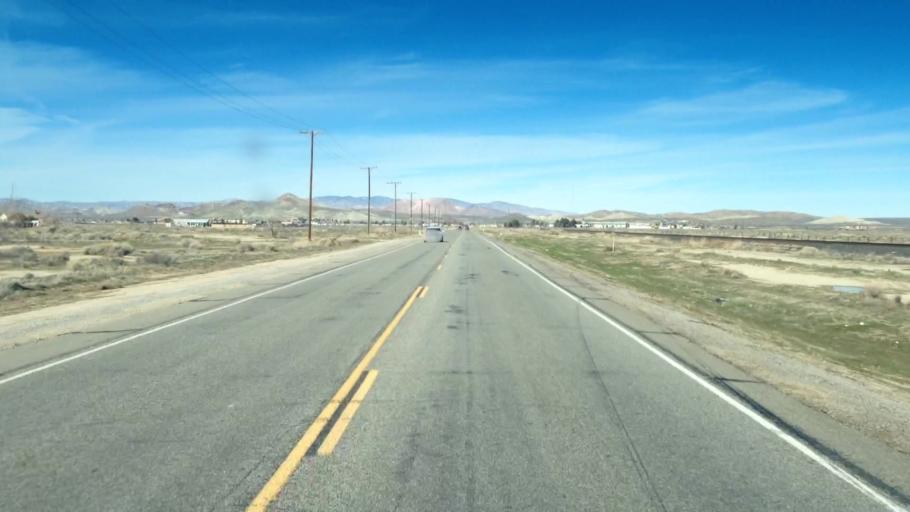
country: US
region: California
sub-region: Kern County
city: Rosamond
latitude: 34.8226
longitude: -118.1563
